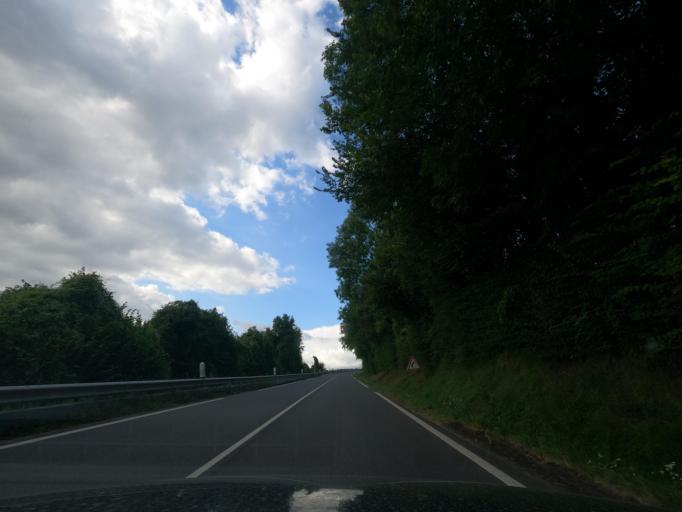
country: FR
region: Lower Normandy
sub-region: Departement de l'Orne
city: Gace
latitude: 48.8113
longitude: 0.3068
